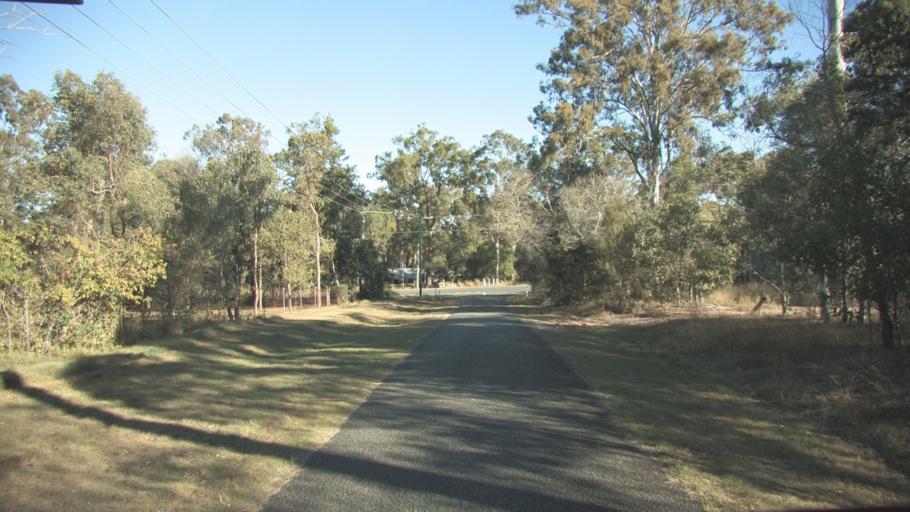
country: AU
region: Queensland
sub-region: Logan
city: North Maclean
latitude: -27.7543
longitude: 153.0053
